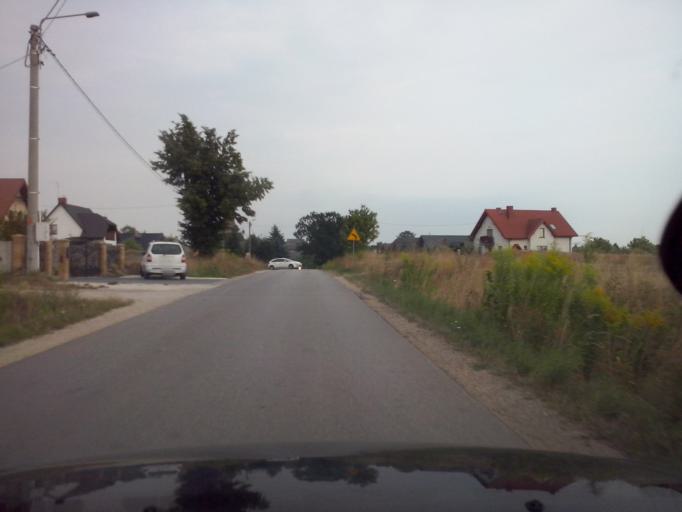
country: PL
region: Swietokrzyskie
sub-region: Powiat kielecki
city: Domaszowice
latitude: 50.8118
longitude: 20.6792
